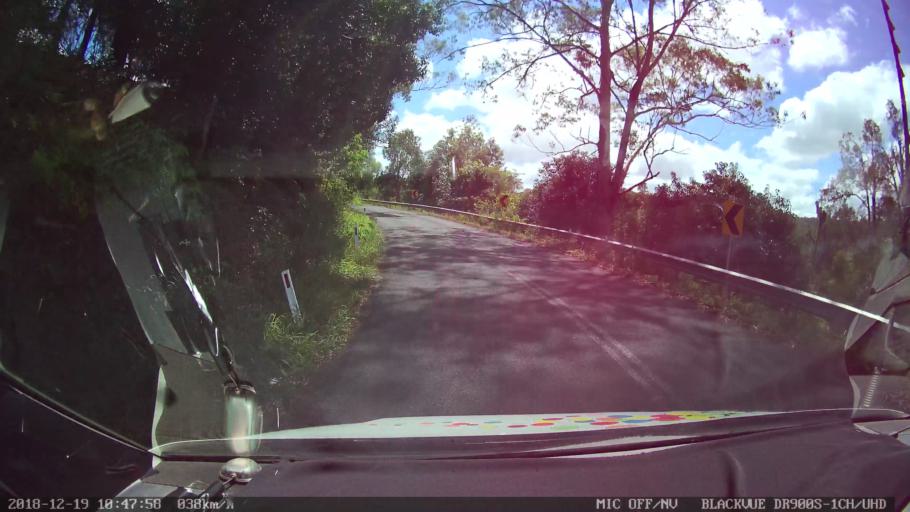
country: AU
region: New South Wales
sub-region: Lismore Municipality
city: Nimbin
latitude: -28.6051
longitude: 153.2096
